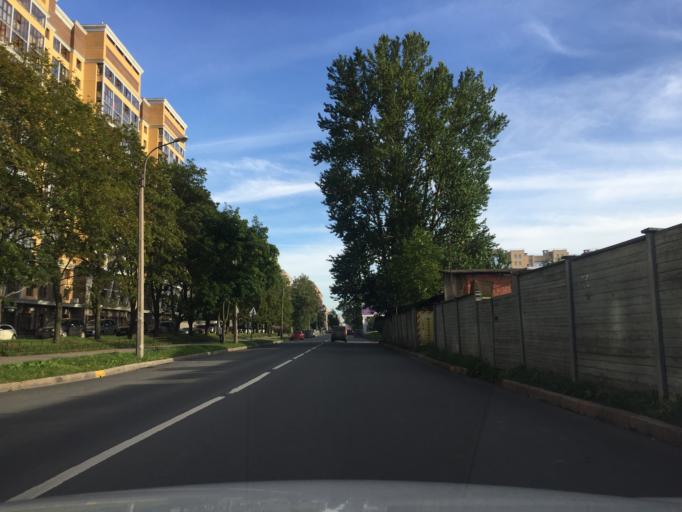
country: RU
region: St.-Petersburg
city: Admiralteisky
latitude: 59.8801
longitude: 30.3131
